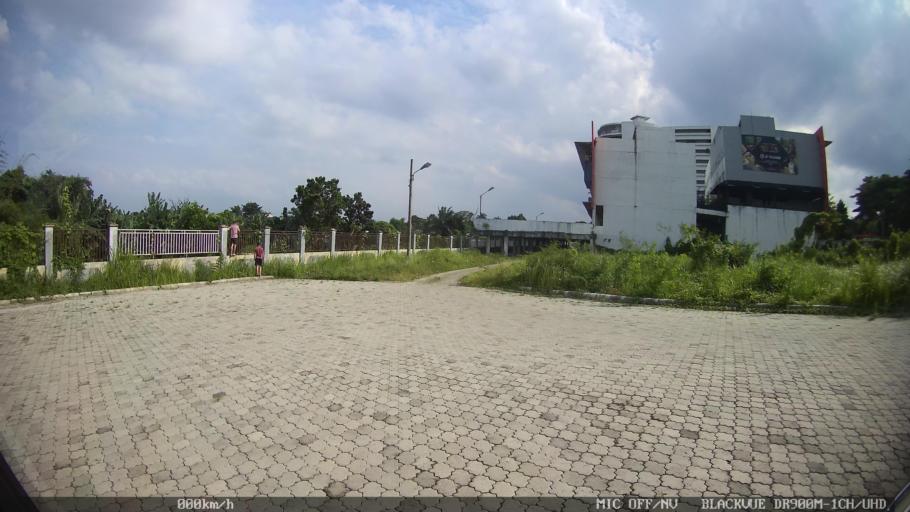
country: ID
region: North Sumatra
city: Medan
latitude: 3.5598
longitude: 98.6843
